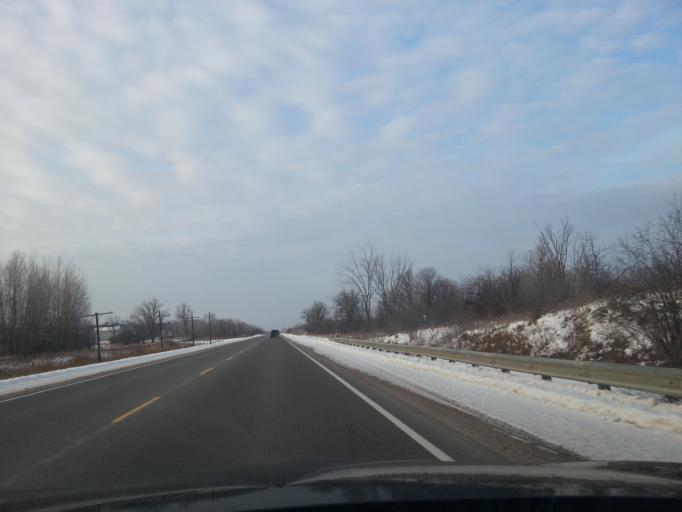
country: CA
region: Ontario
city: Perth
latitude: 44.8984
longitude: -76.2879
